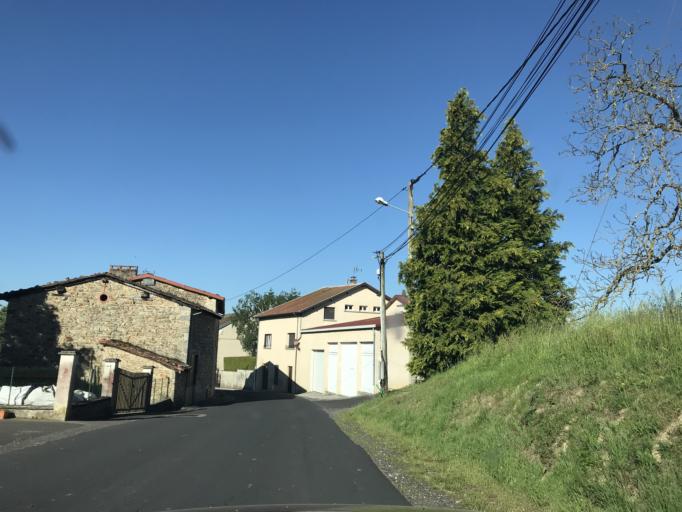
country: FR
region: Auvergne
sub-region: Departement du Puy-de-Dome
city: Job
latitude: 45.6604
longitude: 3.6842
